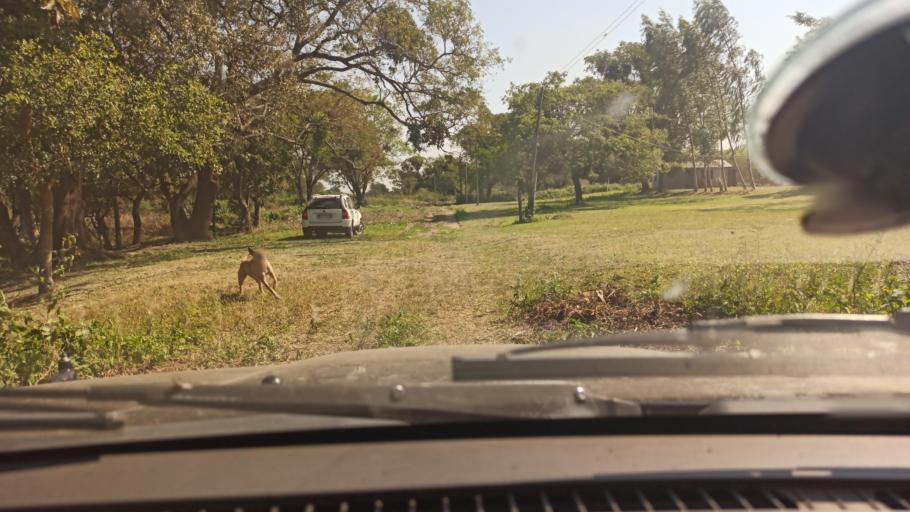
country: PY
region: Asuncion
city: Asuncion
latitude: -25.3530
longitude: -57.6680
